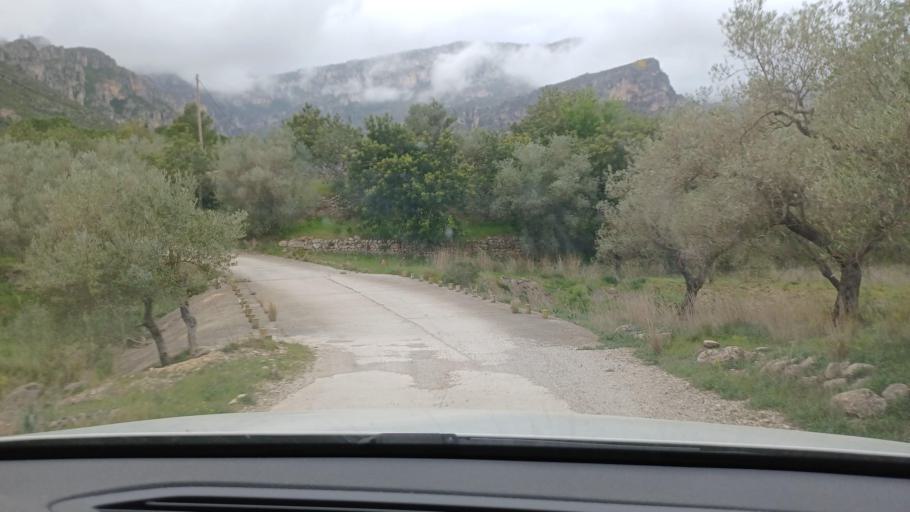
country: ES
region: Catalonia
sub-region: Provincia de Tarragona
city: Mas de Barberans
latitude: 40.8052
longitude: 0.4045
